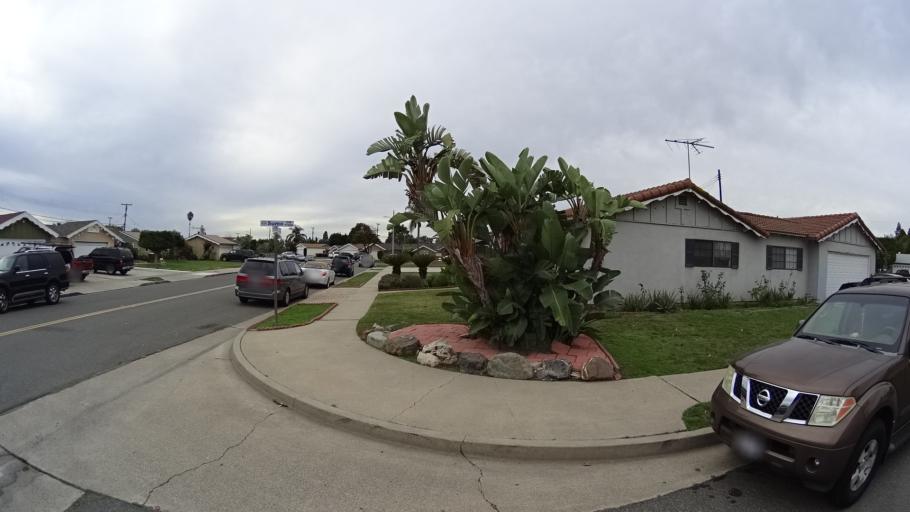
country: US
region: California
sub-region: Orange County
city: Garden Grove
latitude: 33.7806
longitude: -117.9248
